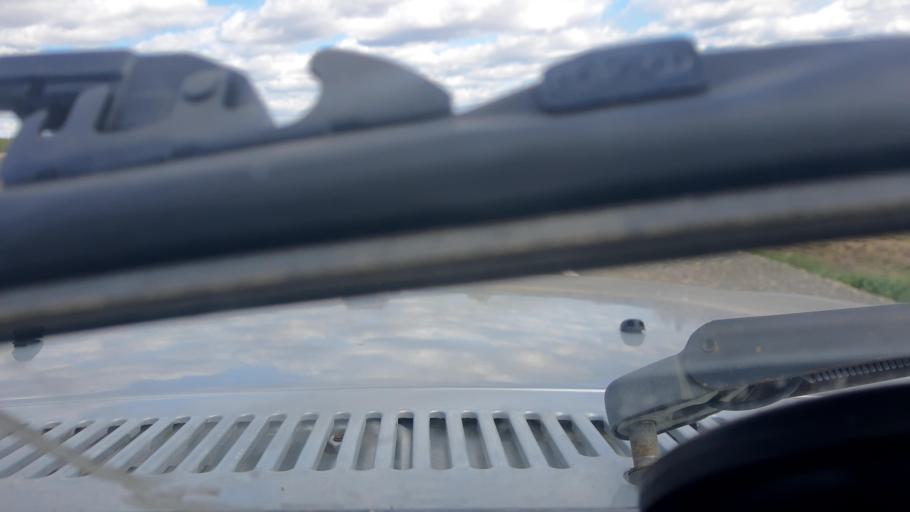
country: RU
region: Bashkortostan
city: Pavlovka
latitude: 55.3253
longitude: 56.3541
